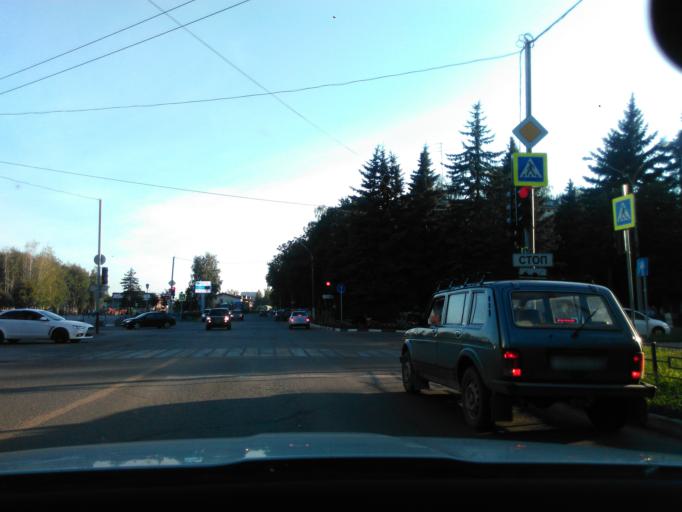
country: RU
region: Tverskaya
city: Konakovo
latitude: 56.7136
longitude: 36.7794
